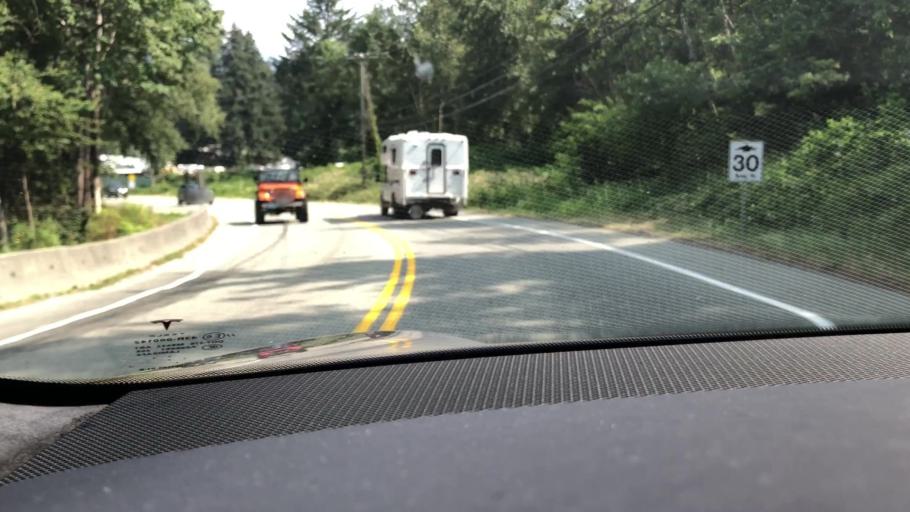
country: CA
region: British Columbia
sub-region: Fraser Valley Regional District
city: Chilliwack
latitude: 49.0948
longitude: -121.9763
